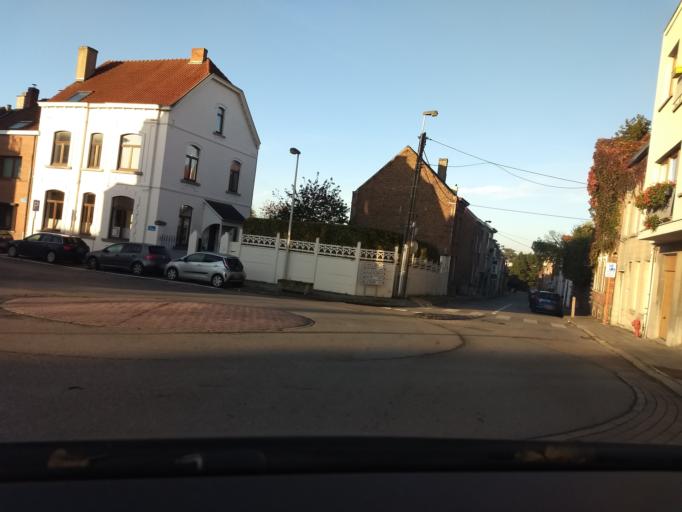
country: BE
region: Wallonia
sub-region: Province du Brabant Wallon
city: Braine-l'Alleud
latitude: 50.6816
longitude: 4.3747
